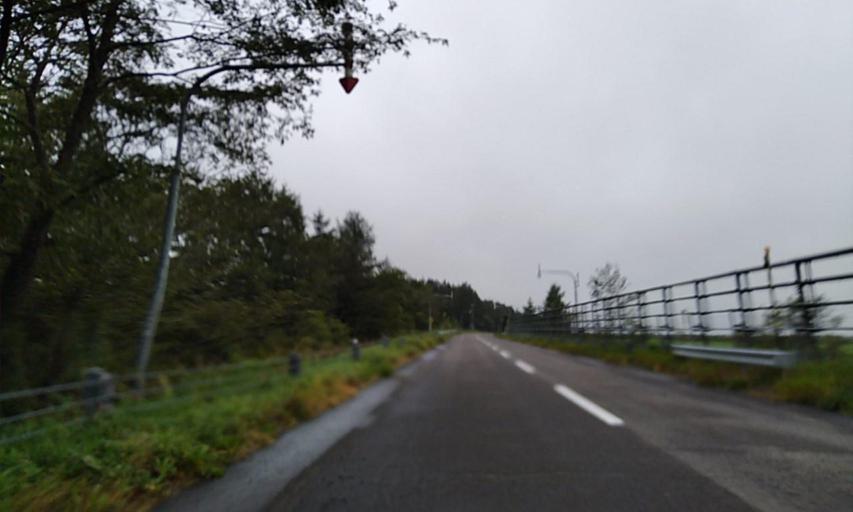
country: JP
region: Hokkaido
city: Shibetsu
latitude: 43.5349
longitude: 144.7063
